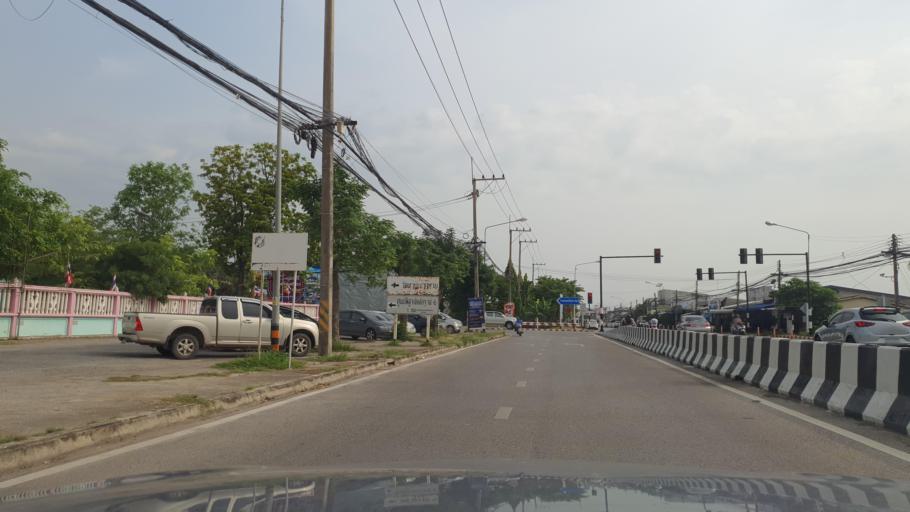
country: TH
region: Phitsanulok
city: Phitsanulok
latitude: 16.8418
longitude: 100.2657
